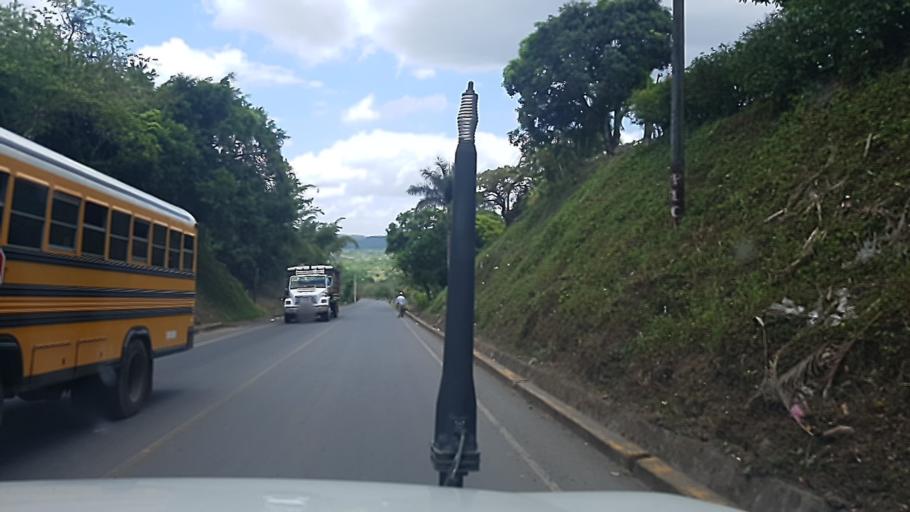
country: NI
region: Chontales
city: Santo Tomas
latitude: 12.0642
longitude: -85.0898
